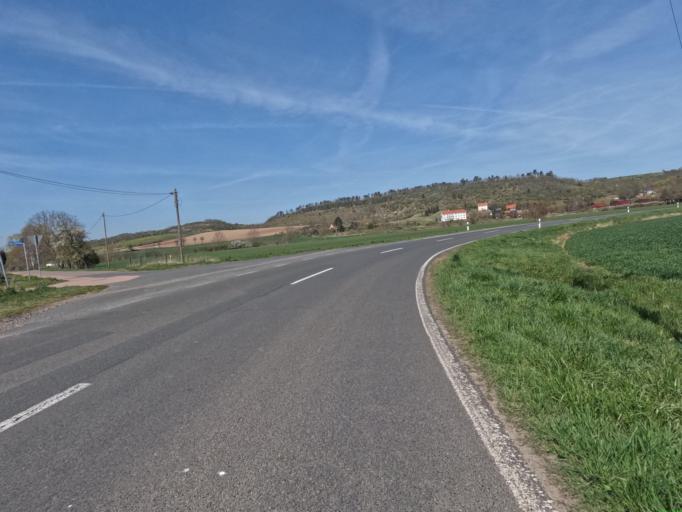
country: DE
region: Saxony-Anhalt
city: Beesenstedt
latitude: 51.6130
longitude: 11.7386
